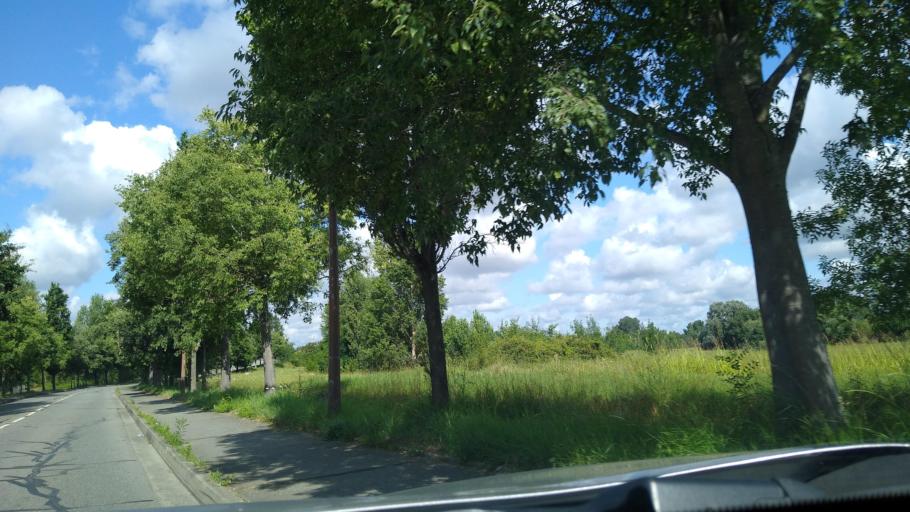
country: FR
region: Midi-Pyrenees
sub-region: Departement de la Haute-Garonne
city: L'Union
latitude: 43.6383
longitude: 1.4810
